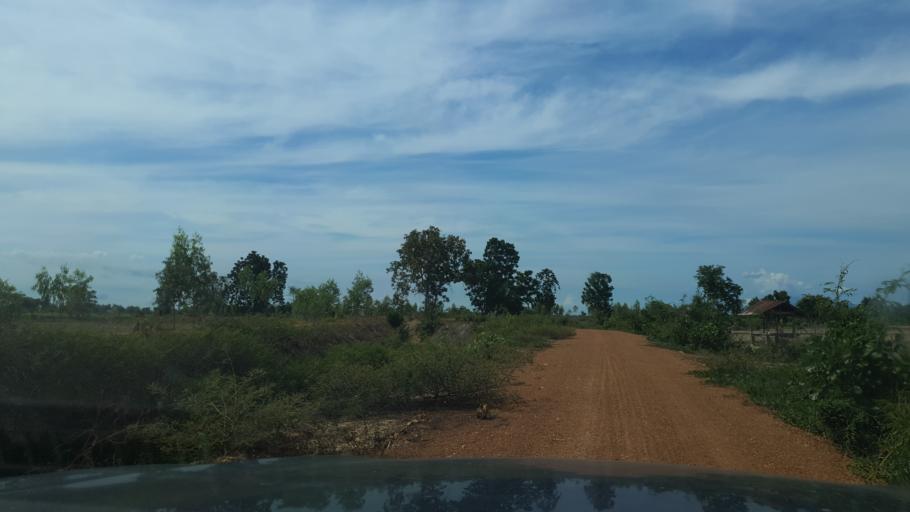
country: TH
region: Sukhothai
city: Thung Saliam
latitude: 17.2510
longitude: 99.6632
